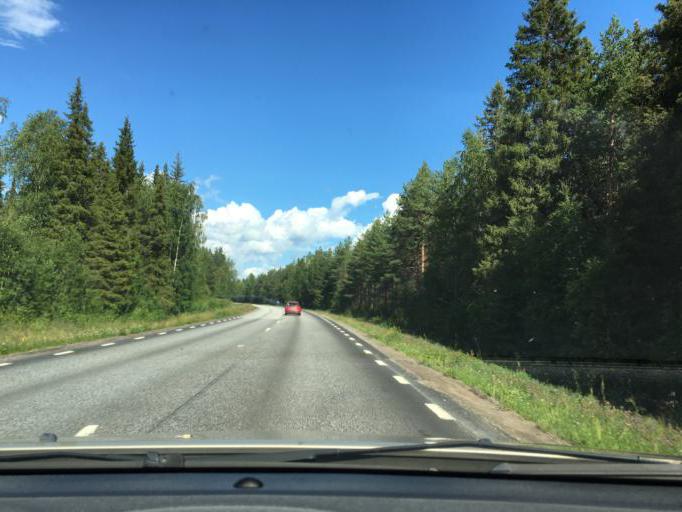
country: SE
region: Norrbotten
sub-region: Overkalix Kommun
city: OEverkalix
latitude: 66.2699
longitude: 22.8190
